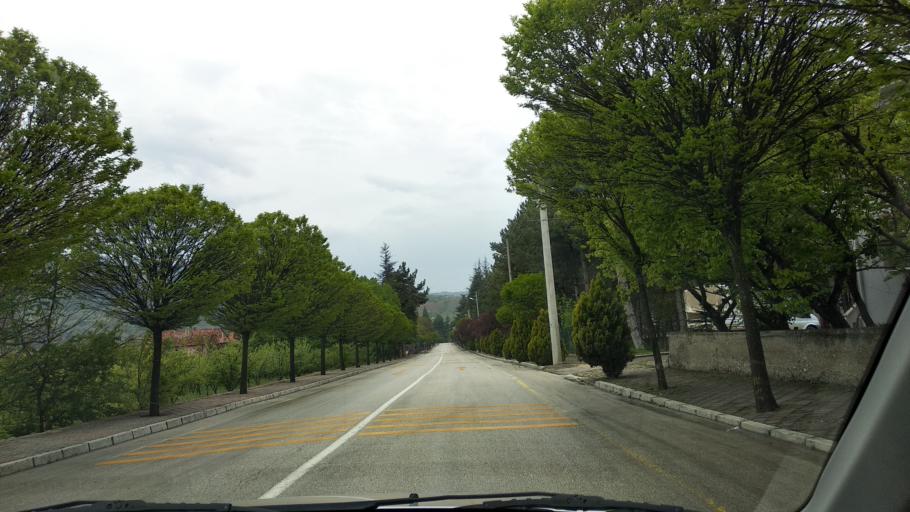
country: TR
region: Bolu
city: Seben
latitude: 40.4148
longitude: 31.5754
